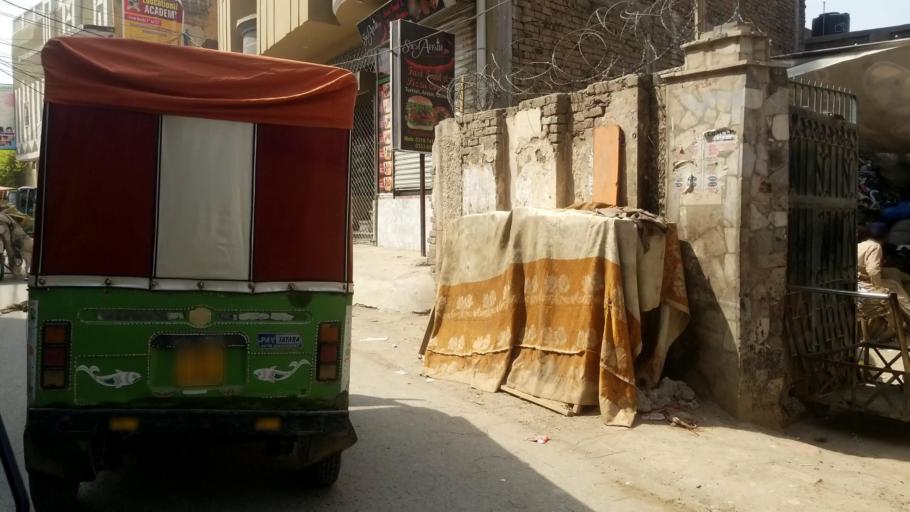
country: PK
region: Khyber Pakhtunkhwa
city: Peshawar
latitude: 33.9859
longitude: 71.5345
